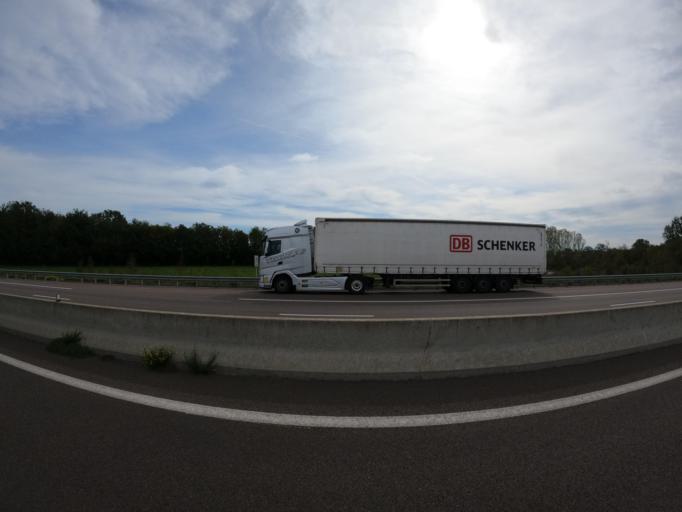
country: FR
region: Bourgogne
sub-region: Departement de Saone-et-Loire
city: Paray-le-Monial
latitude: 46.4822
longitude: 4.1472
